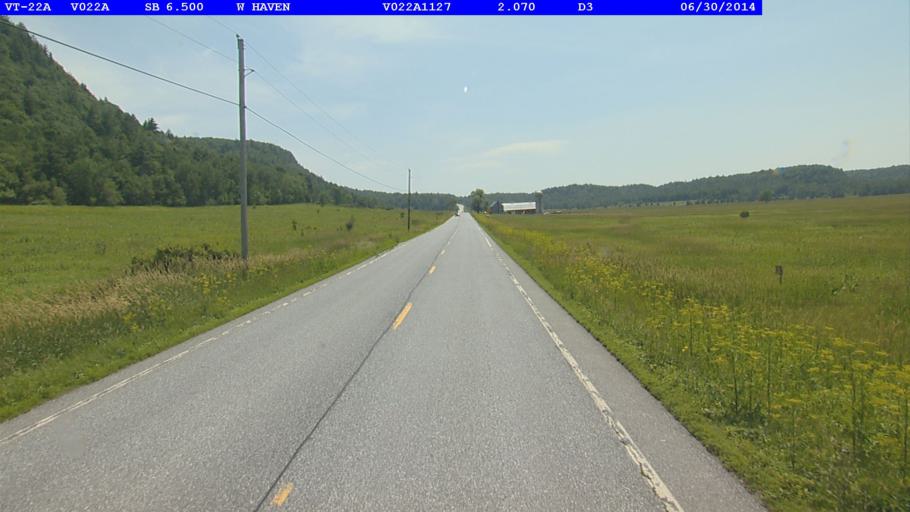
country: US
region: Vermont
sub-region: Rutland County
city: Fair Haven
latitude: 43.6565
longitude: -73.2928
